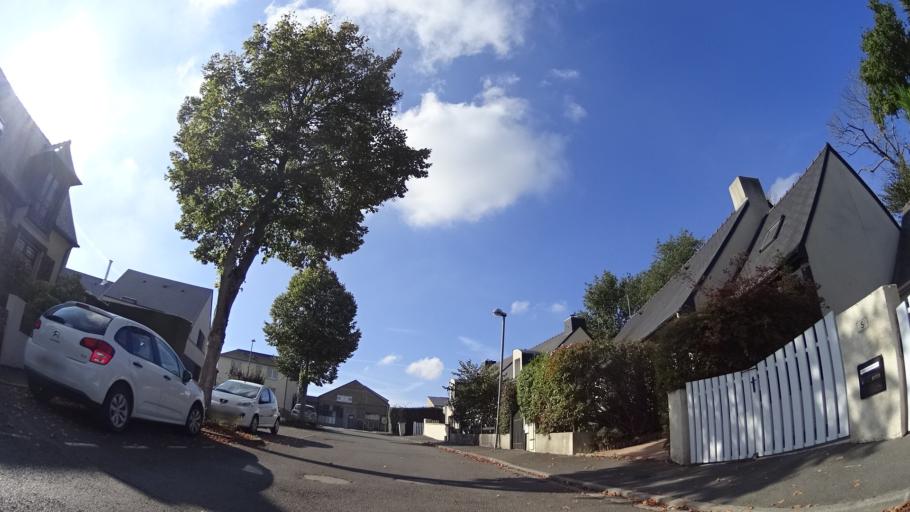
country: FR
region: Brittany
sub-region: Departement d'Ille-et-Vilaine
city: Geveze
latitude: 48.2225
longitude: -1.7920
